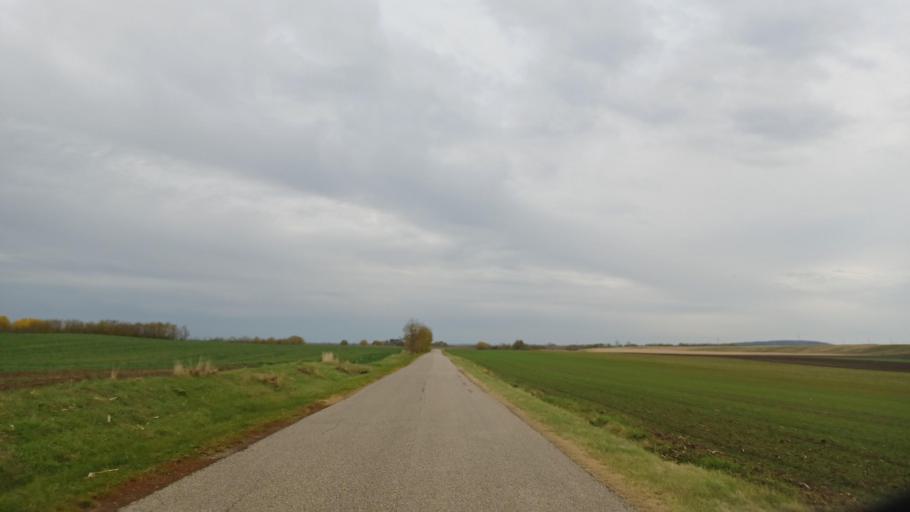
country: HU
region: Tolna
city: Nagydorog
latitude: 46.6559
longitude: 18.6070
